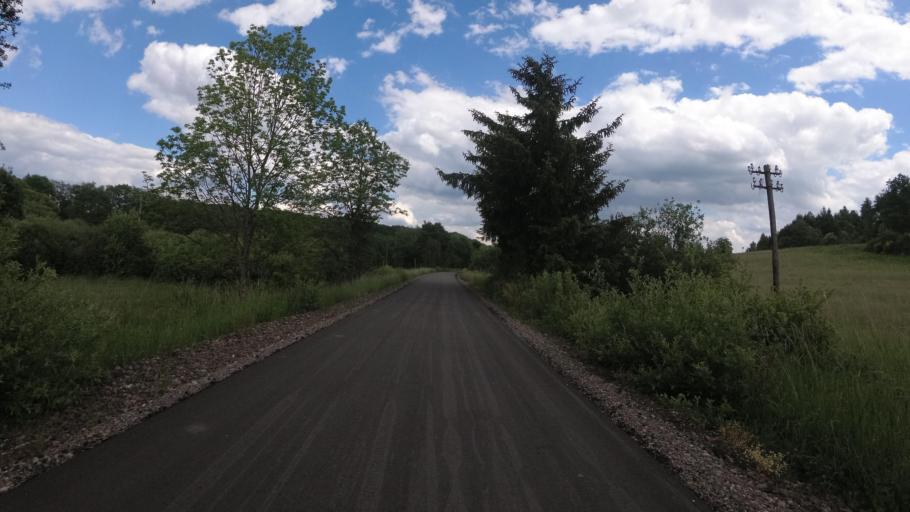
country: DE
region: Rheinland-Pfalz
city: Achtelsbach
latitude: 49.6039
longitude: 7.0491
